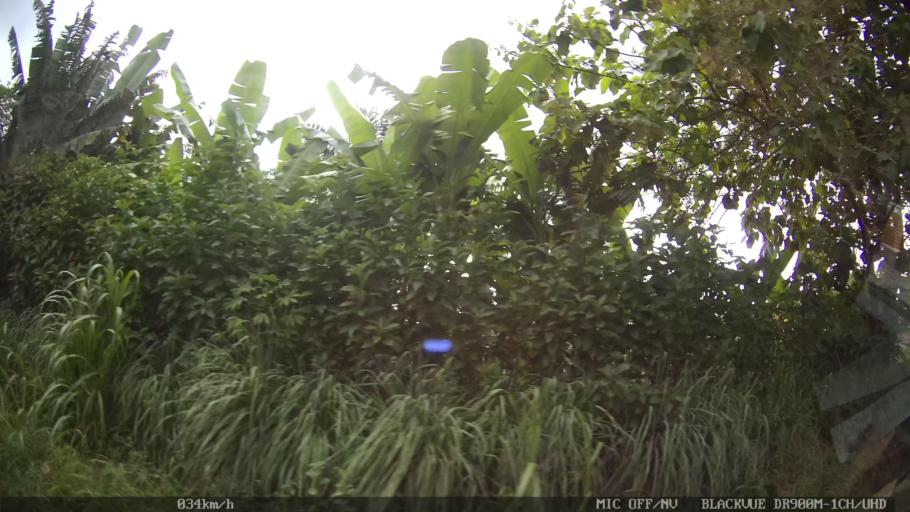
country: ID
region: North Sumatra
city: Sunggal
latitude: 3.5395
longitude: 98.6053
